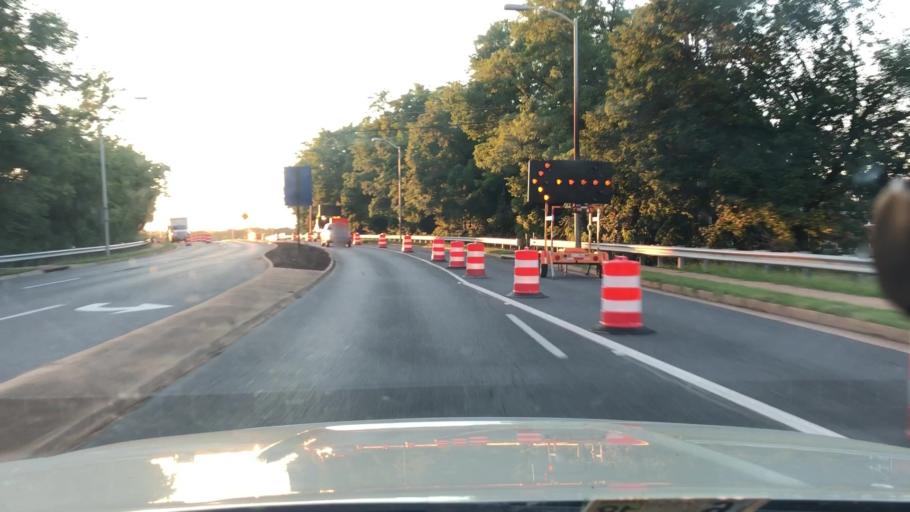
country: US
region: Virginia
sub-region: City of Harrisonburg
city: Harrisonburg
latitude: 38.4430
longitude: -78.8735
